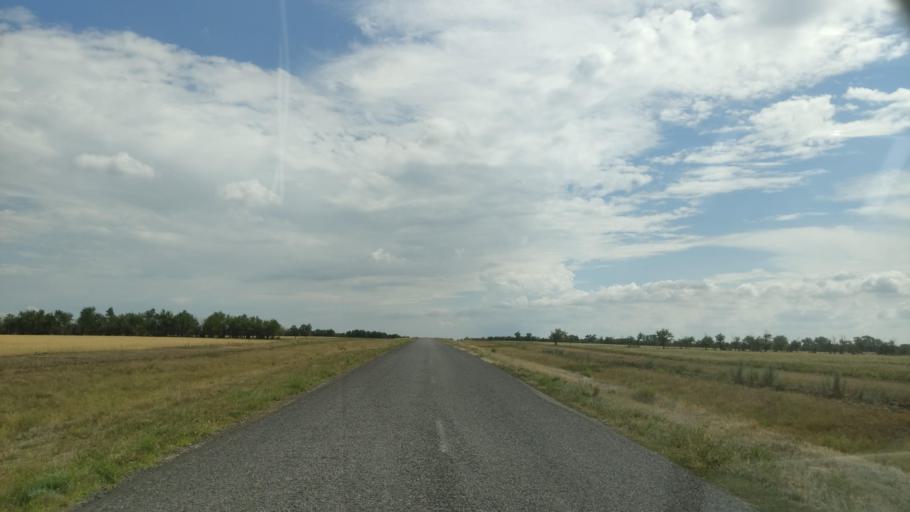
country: KZ
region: Pavlodar
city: Pavlodar
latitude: 52.6366
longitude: 76.9652
